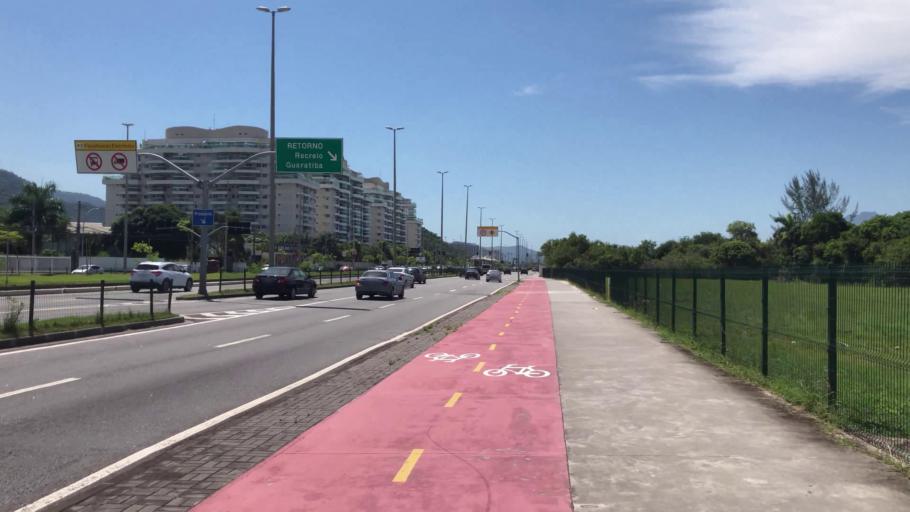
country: BR
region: Rio de Janeiro
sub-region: Nilopolis
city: Nilopolis
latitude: -22.9735
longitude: -43.3920
